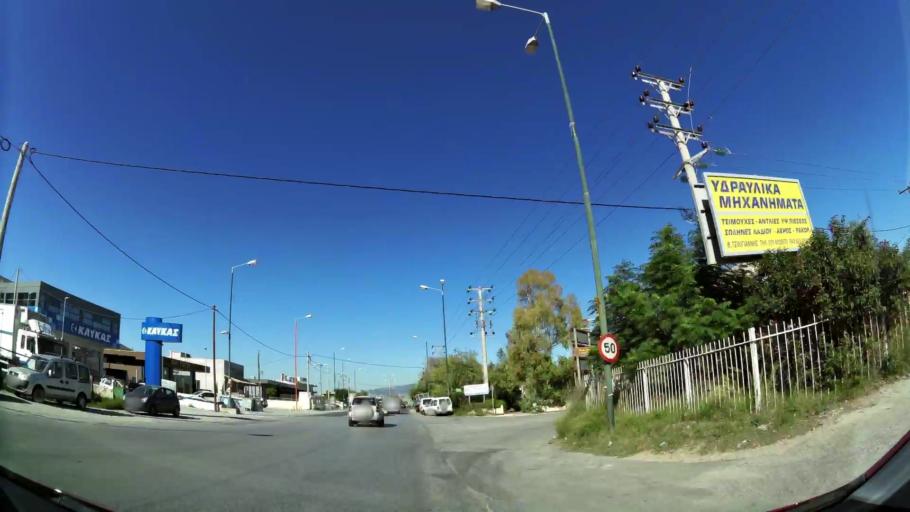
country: GR
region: Attica
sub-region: Nomarchia Anatolikis Attikis
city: Paiania
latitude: 37.9678
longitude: 23.8533
